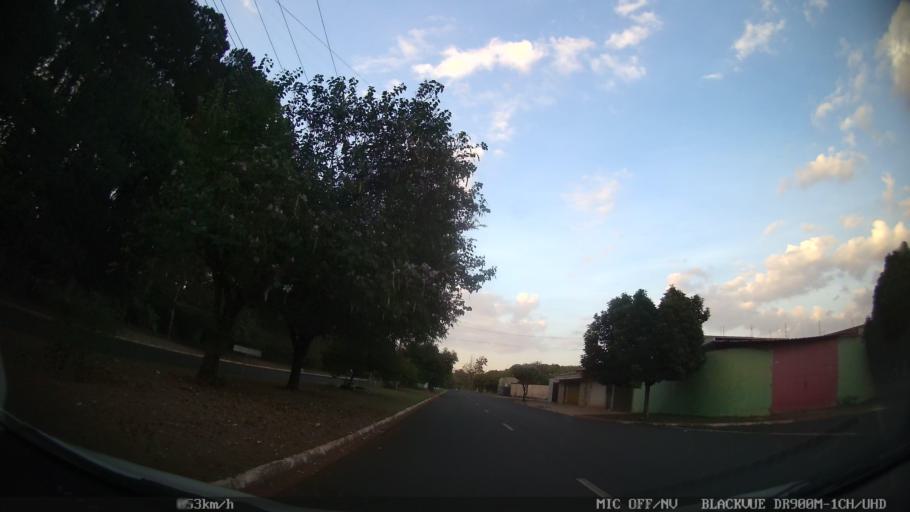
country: BR
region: Sao Paulo
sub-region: Ribeirao Preto
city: Ribeirao Preto
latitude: -21.1287
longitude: -47.8344
